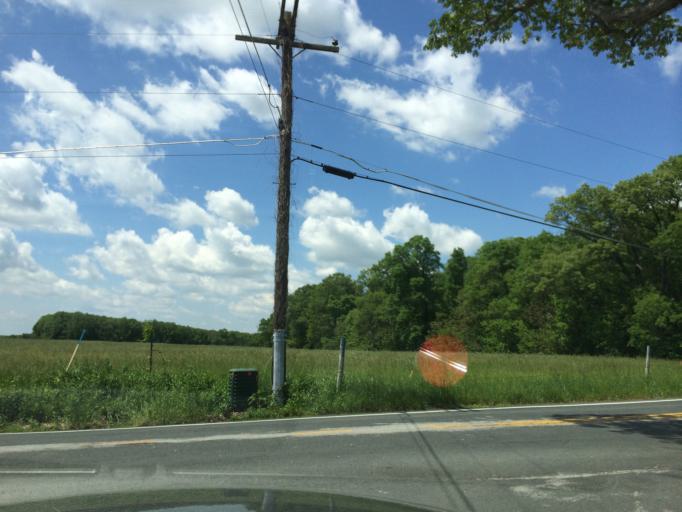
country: US
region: Maryland
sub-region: Carroll County
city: Eldersburg
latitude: 39.4553
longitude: -77.0329
